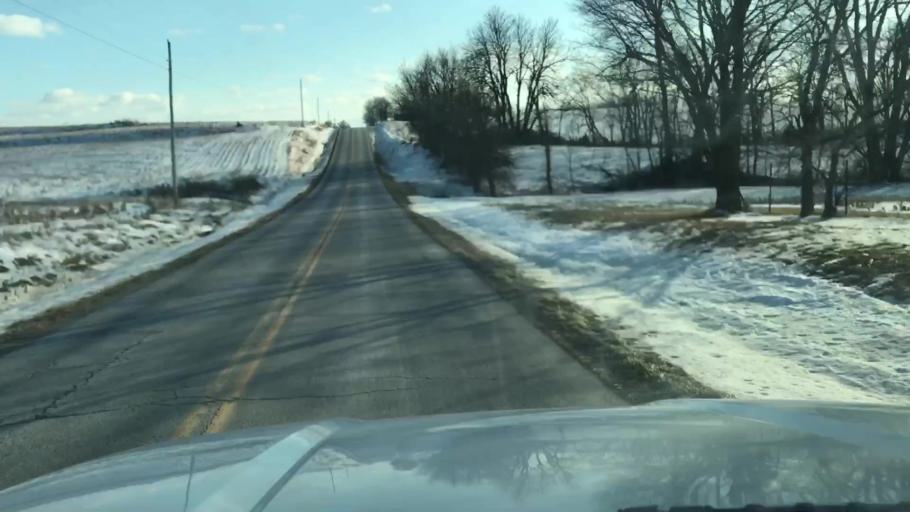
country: US
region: Missouri
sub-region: Holt County
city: Oregon
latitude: 40.0546
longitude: -94.9749
